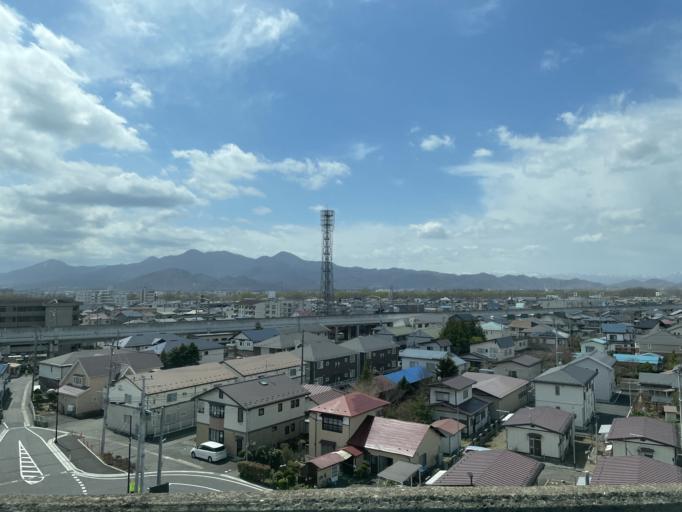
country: JP
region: Iwate
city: Morioka-shi
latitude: 39.7092
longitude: 141.1277
